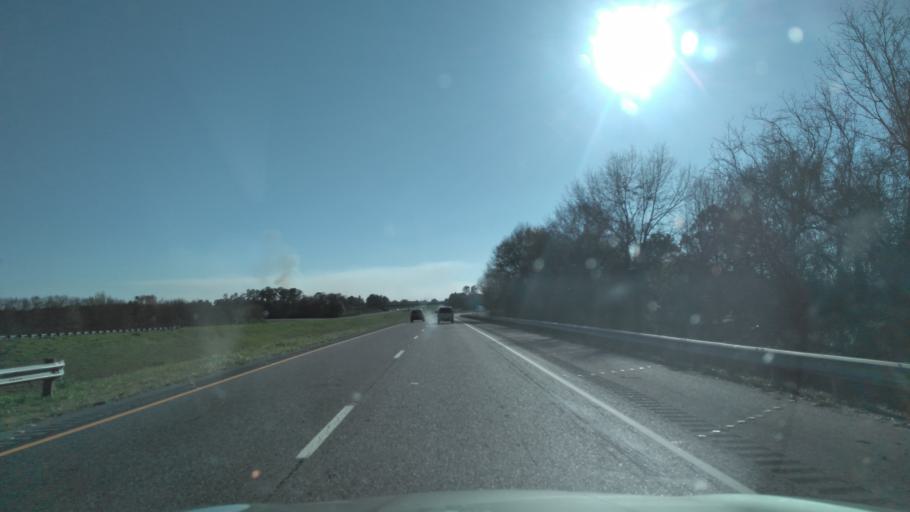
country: US
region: Alabama
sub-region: Escambia County
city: Atmore
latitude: 31.0889
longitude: -87.5280
